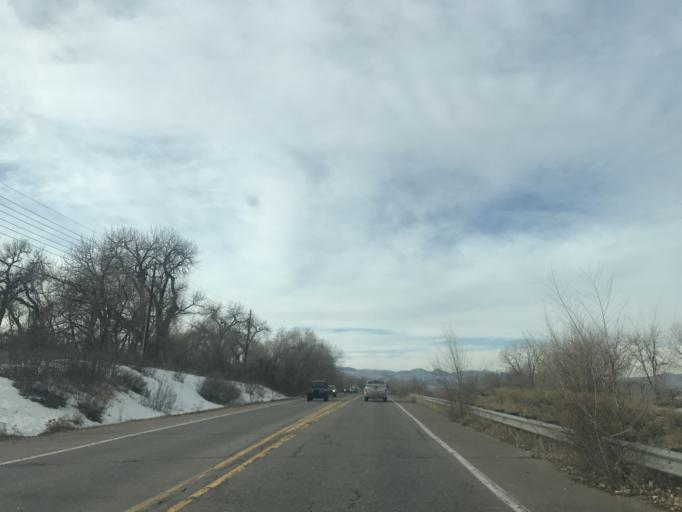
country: US
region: Colorado
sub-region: Douglas County
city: Highlands Ranch
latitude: 39.5645
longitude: -105.0048
